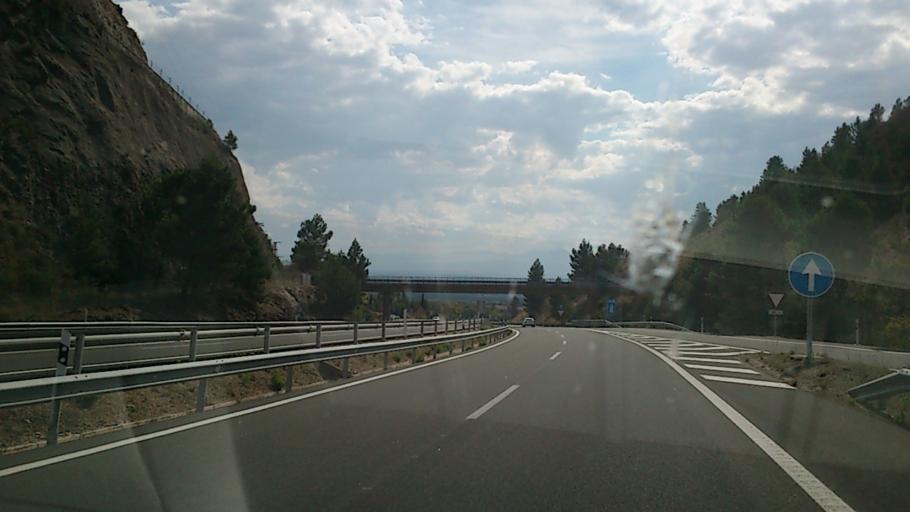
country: ES
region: La Rioja
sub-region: Provincia de La Rioja
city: Brinas
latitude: 42.6168
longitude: -2.8557
